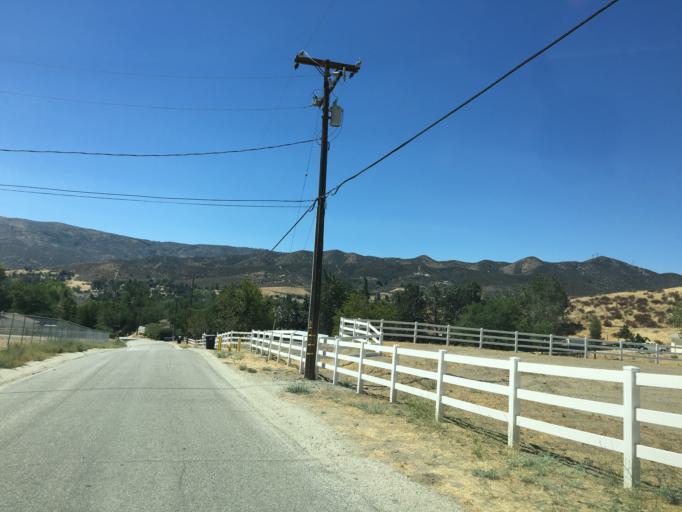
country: US
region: California
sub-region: Los Angeles County
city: Leona Valley
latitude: 34.6215
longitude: -118.2888
